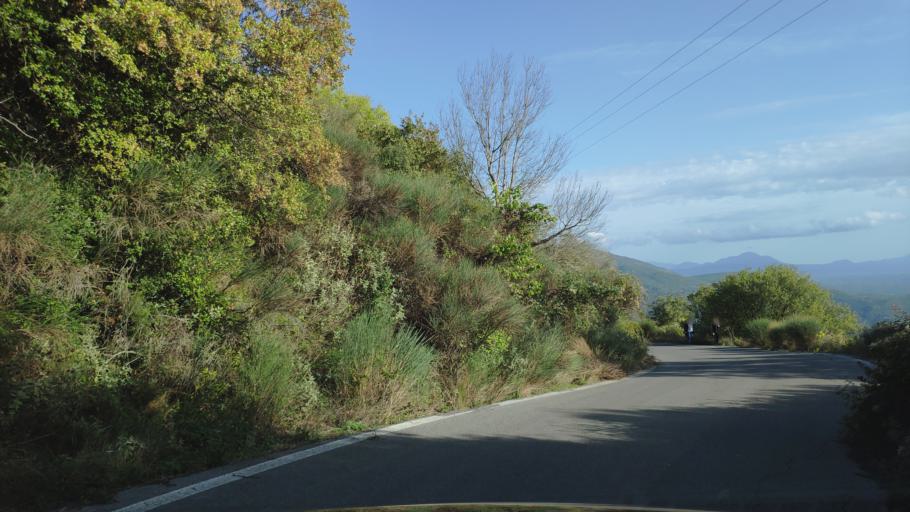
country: GR
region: Peloponnese
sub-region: Nomos Arkadias
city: Dimitsana
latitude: 37.5606
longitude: 22.0324
